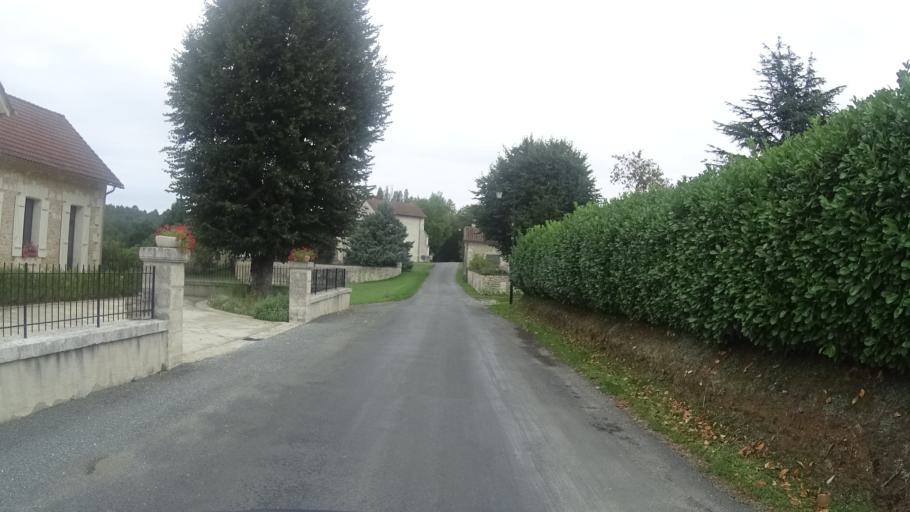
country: FR
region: Aquitaine
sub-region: Departement de la Dordogne
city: Neuvic
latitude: 45.0285
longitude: 0.5110
